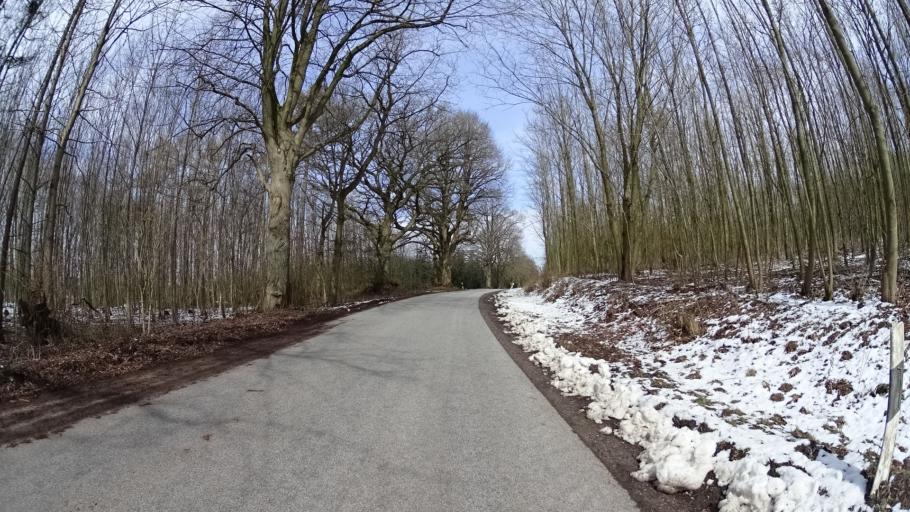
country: DE
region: Schleswig-Holstein
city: Stolpe
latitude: 54.1477
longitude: 10.2323
